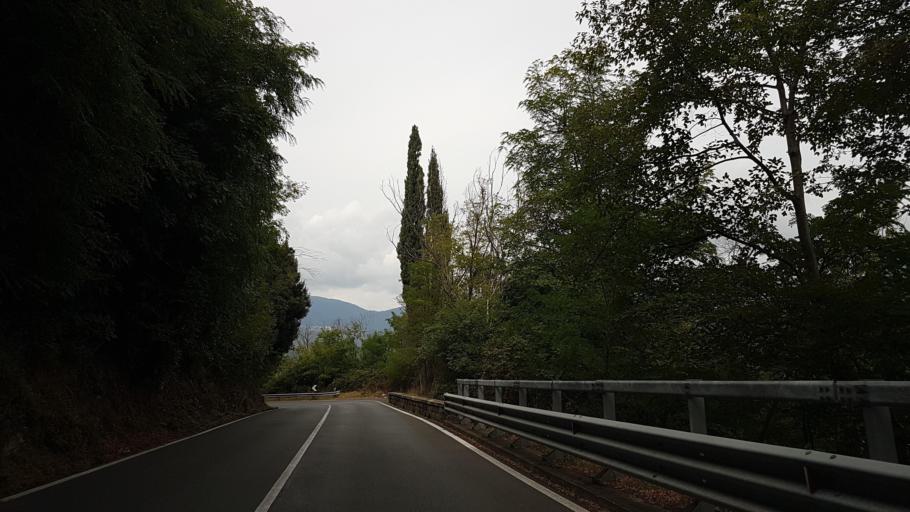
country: IT
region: Liguria
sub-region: Provincia di Genova
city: Casarza Ligure
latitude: 44.2608
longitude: 9.4513
